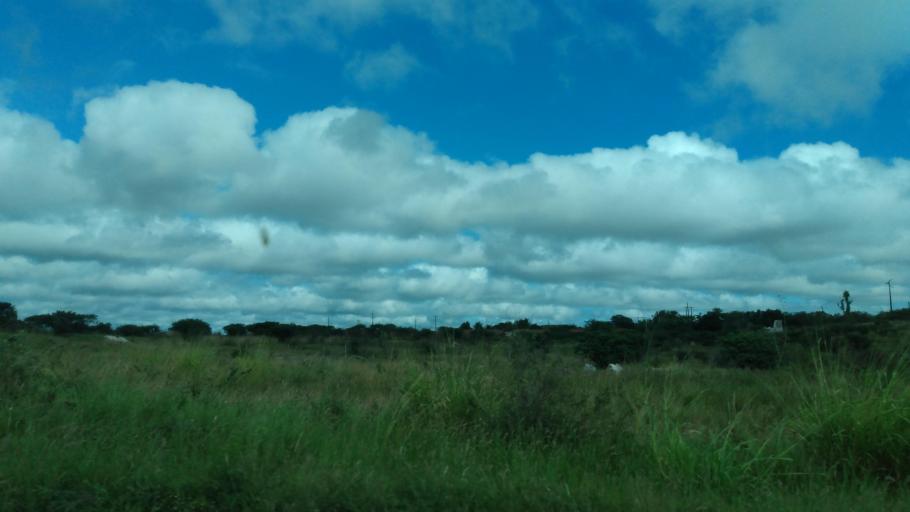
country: BR
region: Pernambuco
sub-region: Caruaru
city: Caruaru
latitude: -8.3051
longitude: -35.9893
